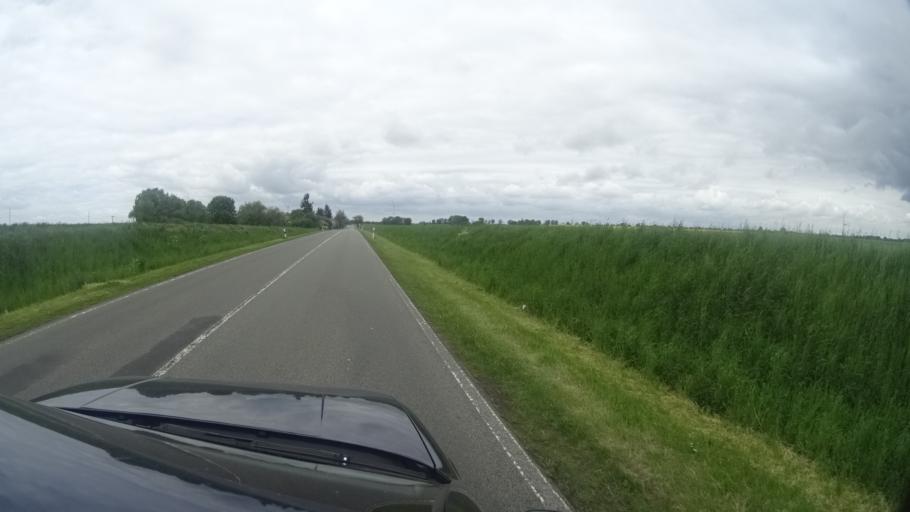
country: DE
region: Brandenburg
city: Fehrbellin
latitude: 52.8557
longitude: 12.7777
